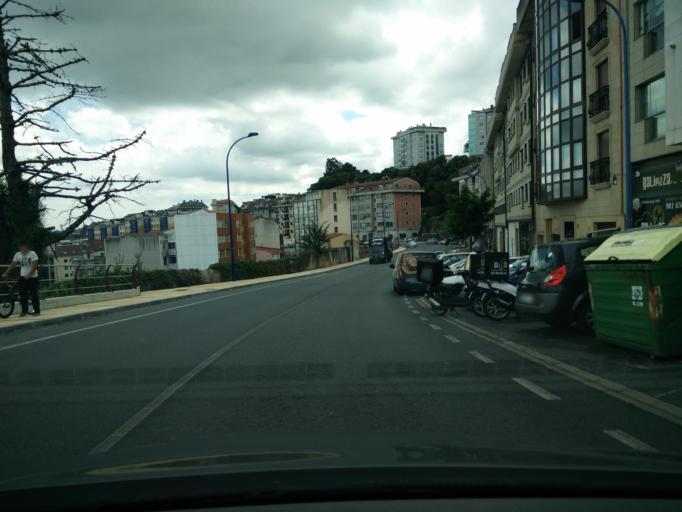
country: ES
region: Galicia
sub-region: Provincia da Coruna
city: Culleredo
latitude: 43.3240
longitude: -8.3816
